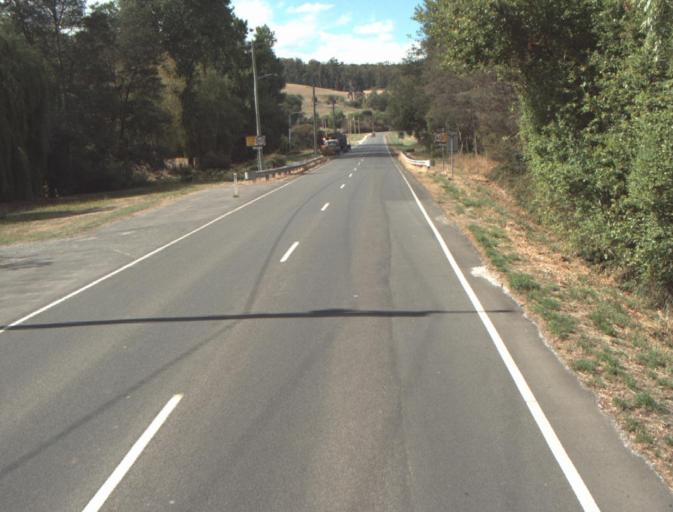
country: AU
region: Tasmania
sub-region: Launceston
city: Mayfield
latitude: -41.2551
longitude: 147.2161
